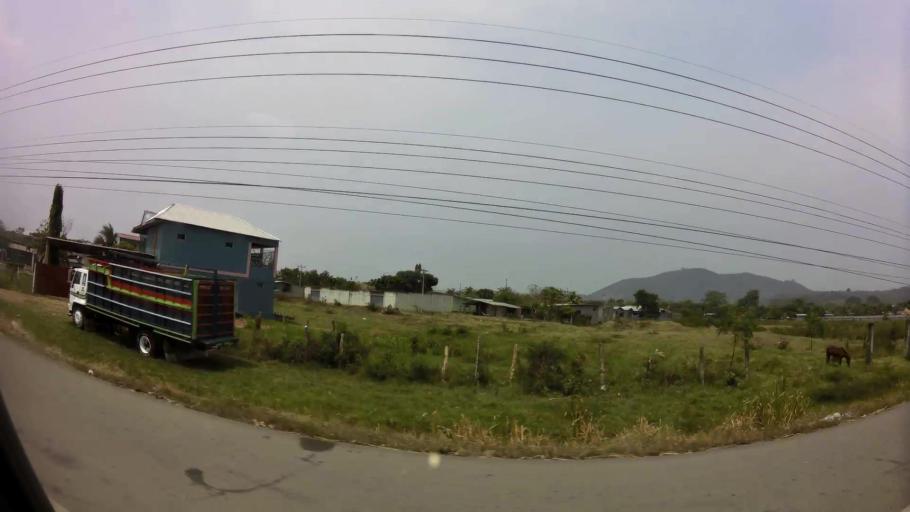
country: HN
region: Cortes
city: El Plan
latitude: 15.3005
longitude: -87.9826
